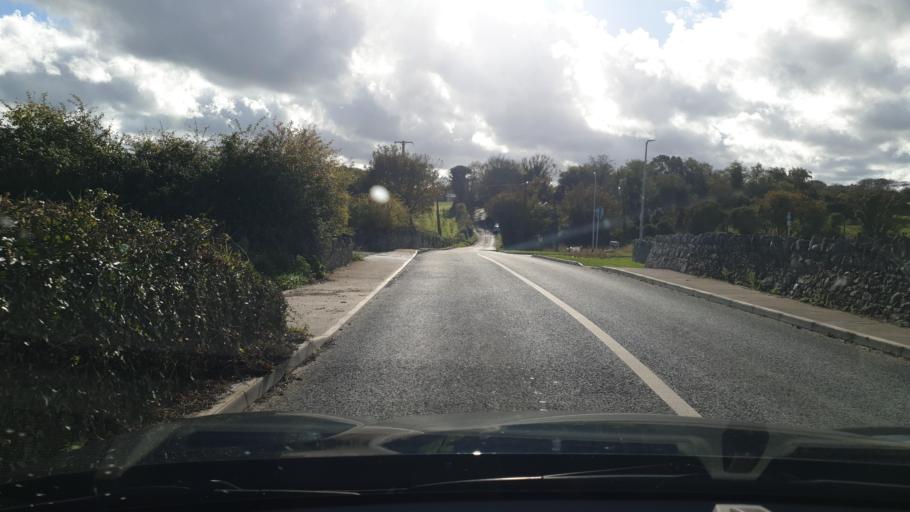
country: IE
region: Leinster
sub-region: Fingal County
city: Skerries
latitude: 53.5687
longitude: -6.1090
